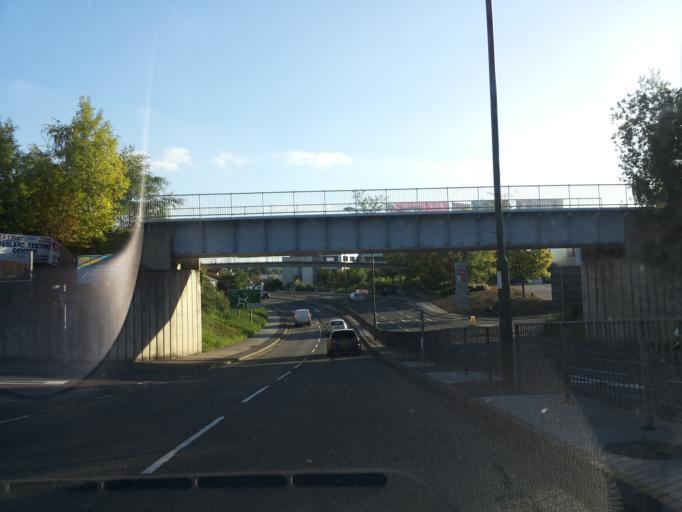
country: GB
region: England
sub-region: Derbyshire
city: Chesterfield
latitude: 53.2330
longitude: -1.4234
